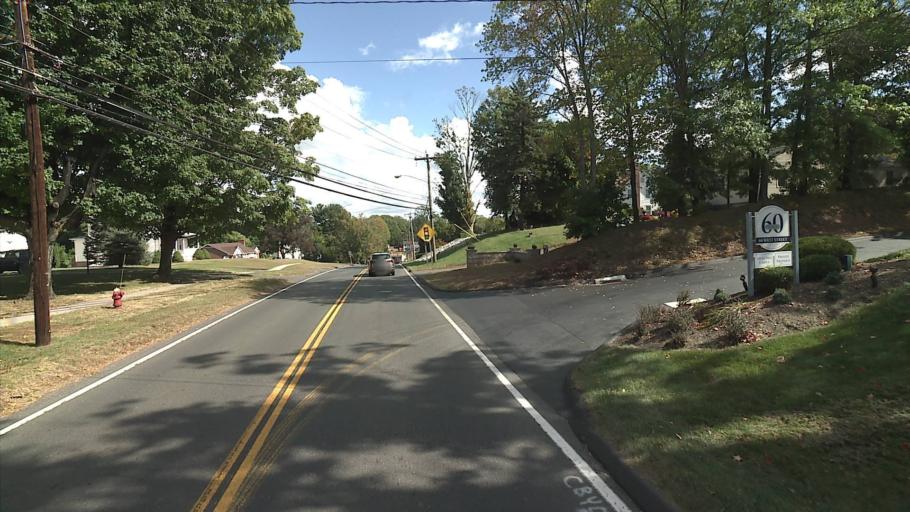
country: US
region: Connecticut
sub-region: Middlesex County
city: Cromwell
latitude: 41.6541
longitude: -72.6434
